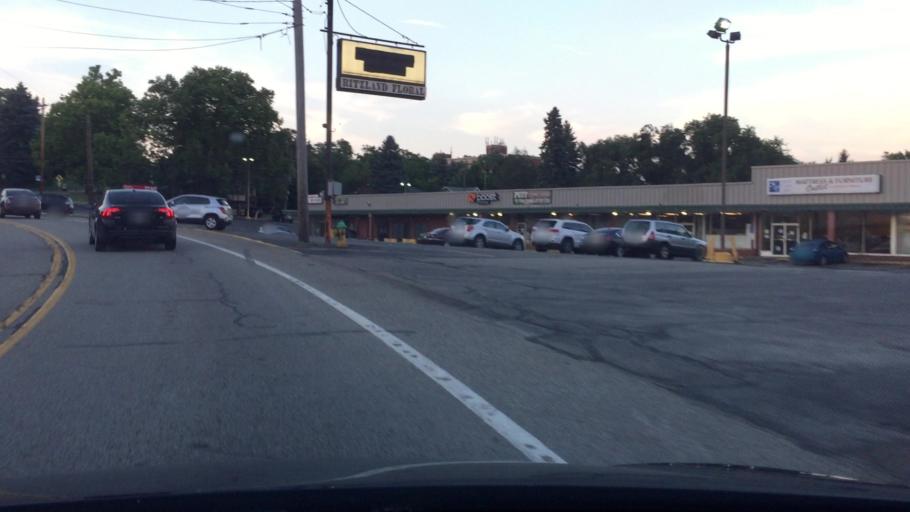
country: US
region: Pennsylvania
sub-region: Allegheny County
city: Churchill
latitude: 40.4613
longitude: -79.8411
